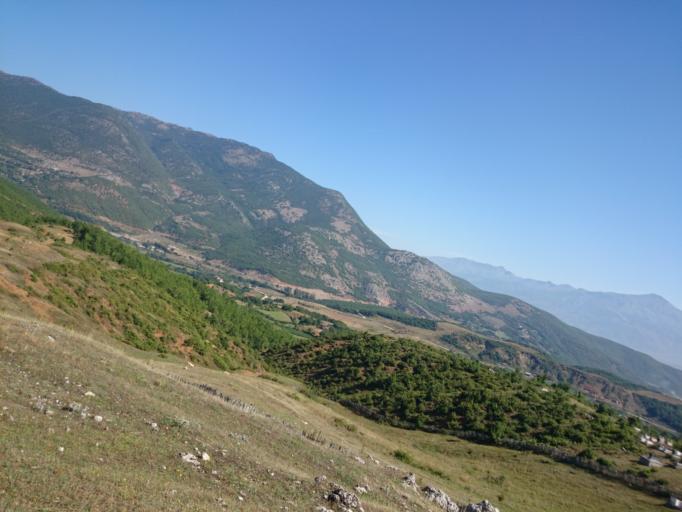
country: AL
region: Diber
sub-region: Rrethi i Bulqizes
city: Zerqan
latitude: 41.4940
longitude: 20.3835
